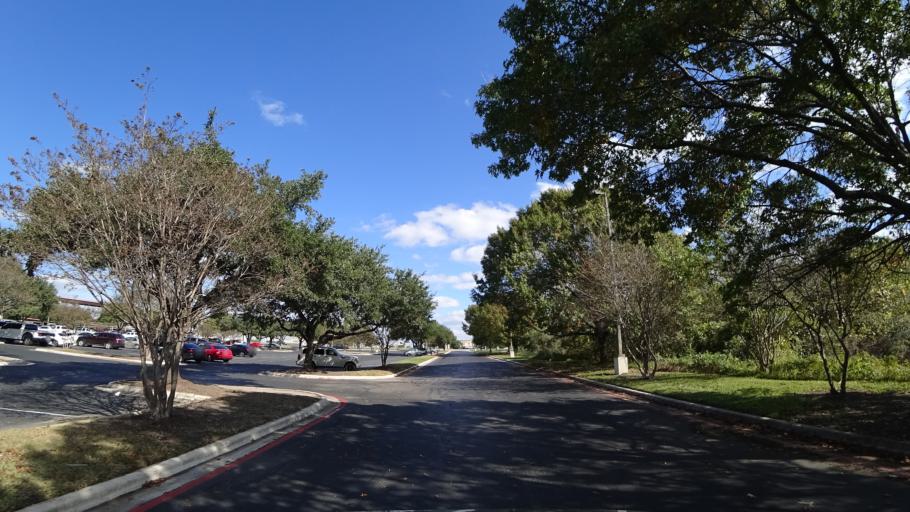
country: US
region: Texas
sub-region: Williamson County
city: Round Rock
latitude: 30.4774
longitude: -97.6752
